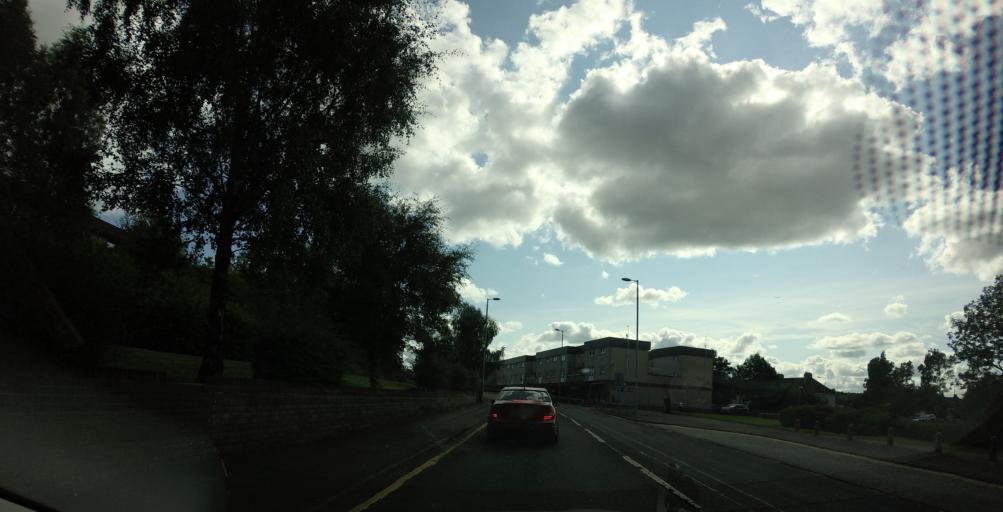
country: GB
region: Scotland
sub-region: North Lanarkshire
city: Coatbridge
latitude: 55.8531
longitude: -4.0475
